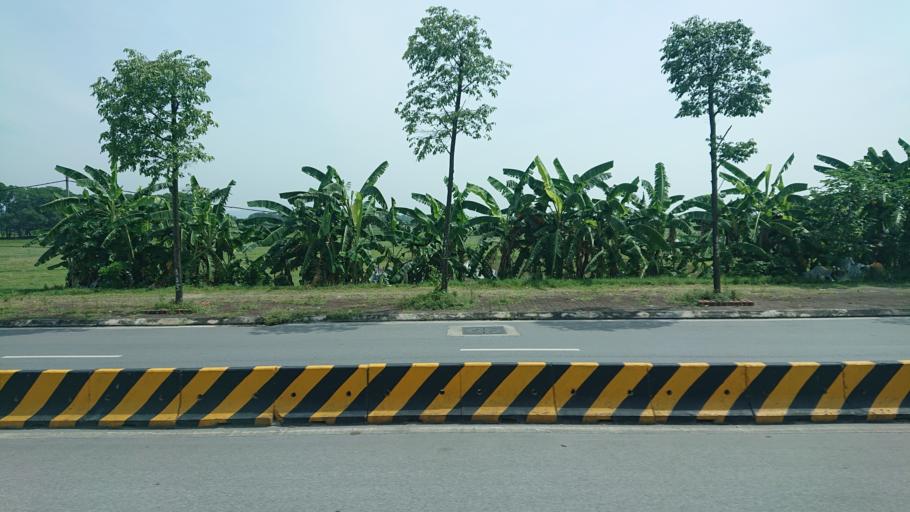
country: VN
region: Ha Noi
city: Soc Son
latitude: 21.2067
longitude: 105.8254
